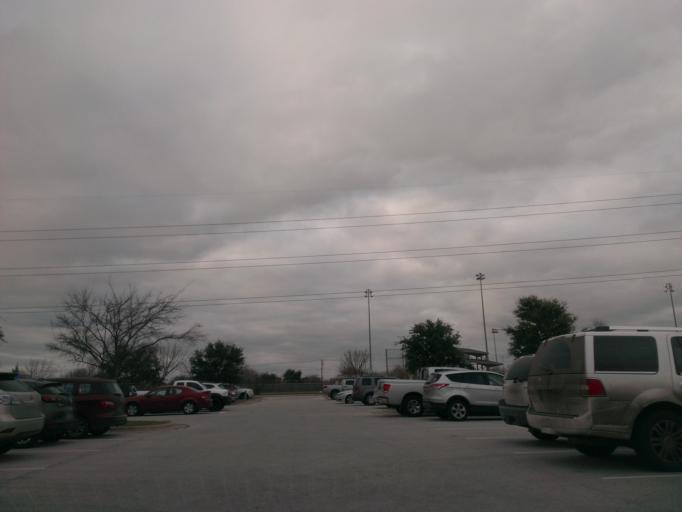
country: US
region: Texas
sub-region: Williamson County
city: Round Rock
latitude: 30.5445
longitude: -97.6194
